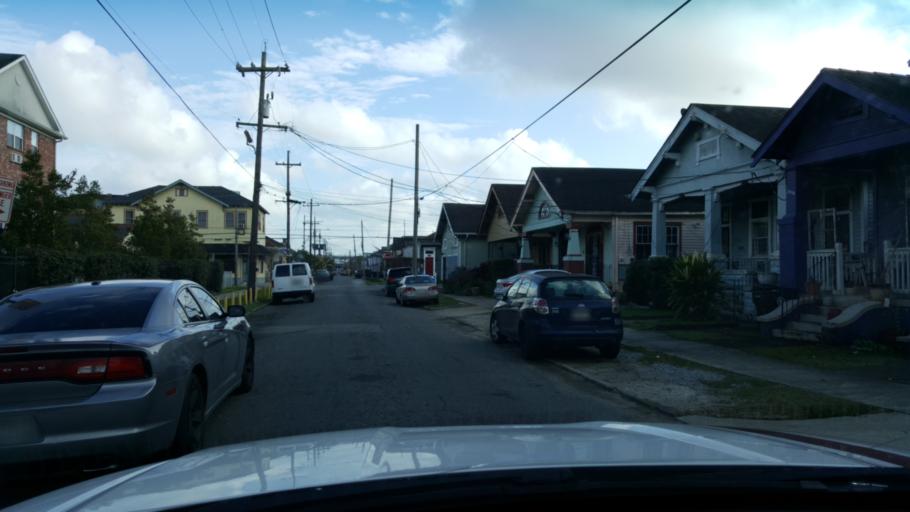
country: US
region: Louisiana
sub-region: Orleans Parish
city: New Orleans
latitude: 29.9767
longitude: -90.0715
